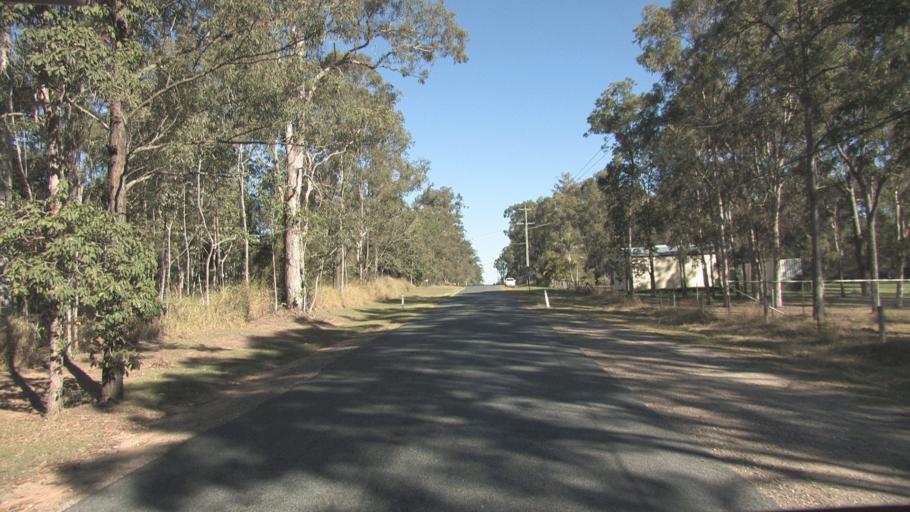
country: AU
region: Queensland
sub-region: Logan
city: Park Ridge South
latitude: -27.7249
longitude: 153.0125
